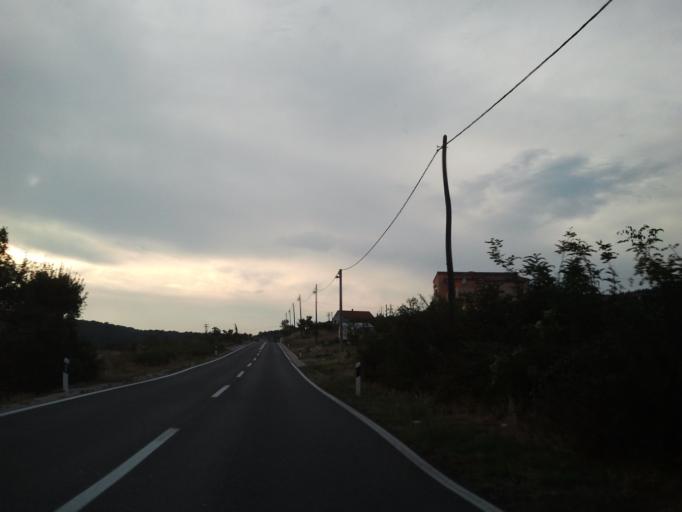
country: HR
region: Zadarska
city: Posedarje
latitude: 44.2220
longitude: 15.4471
